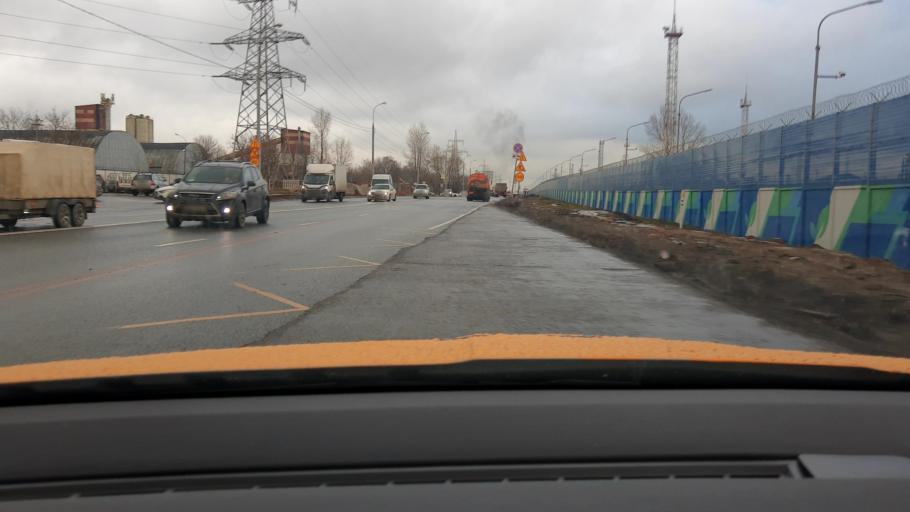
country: RU
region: Moscow
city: Kapotnya
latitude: 55.6582
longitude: 37.7996
